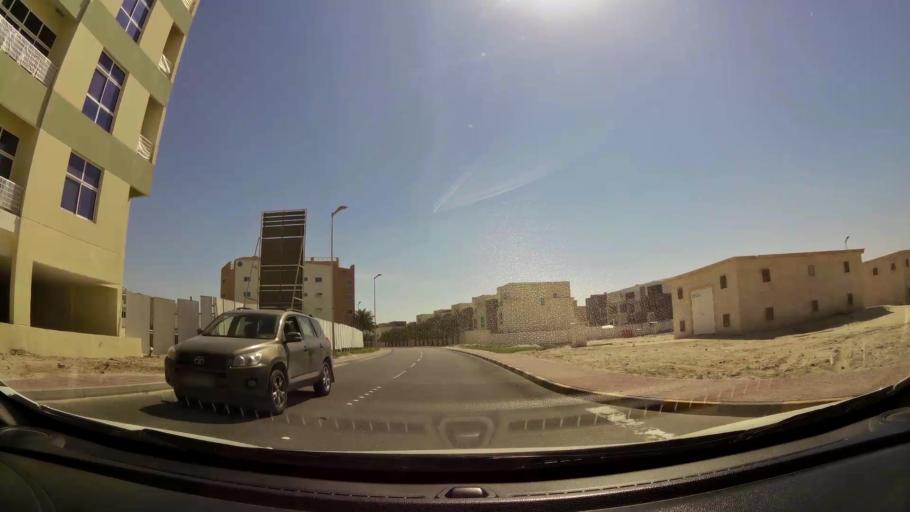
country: BH
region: Muharraq
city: Al Hadd
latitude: 26.2982
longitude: 50.6580
